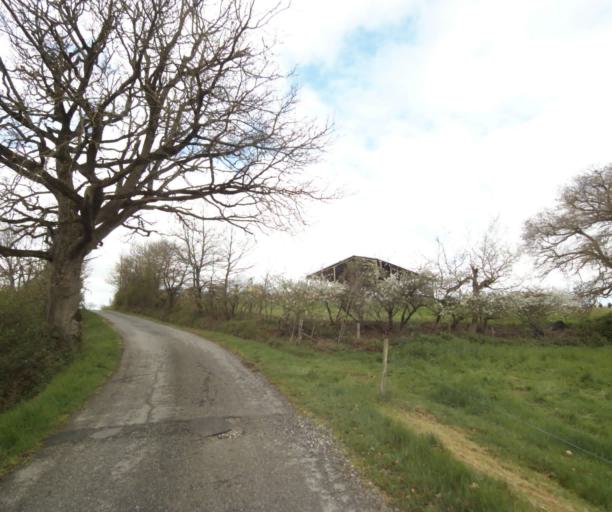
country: FR
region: Midi-Pyrenees
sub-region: Departement de l'Ariege
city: Saverdun
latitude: 43.2180
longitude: 1.5396
